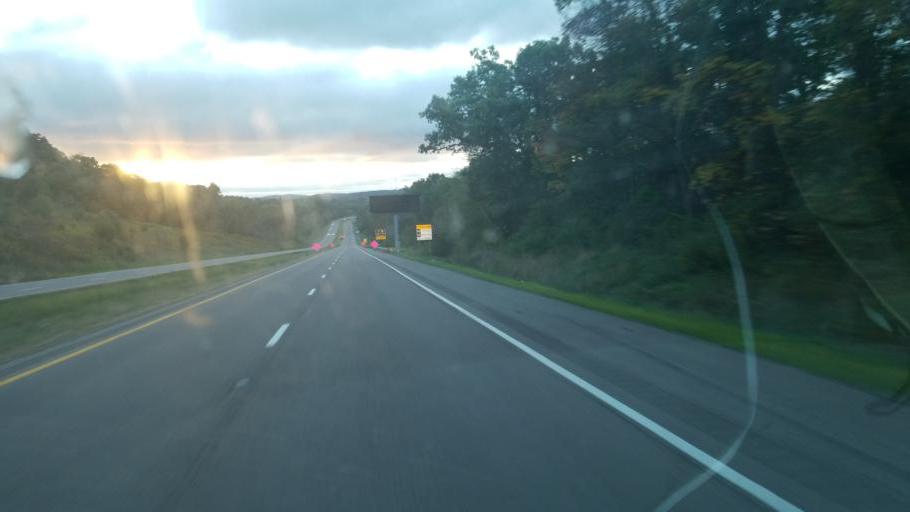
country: US
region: West Virginia
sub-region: Preston County
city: Terra Alta
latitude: 39.6604
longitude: -79.4625
